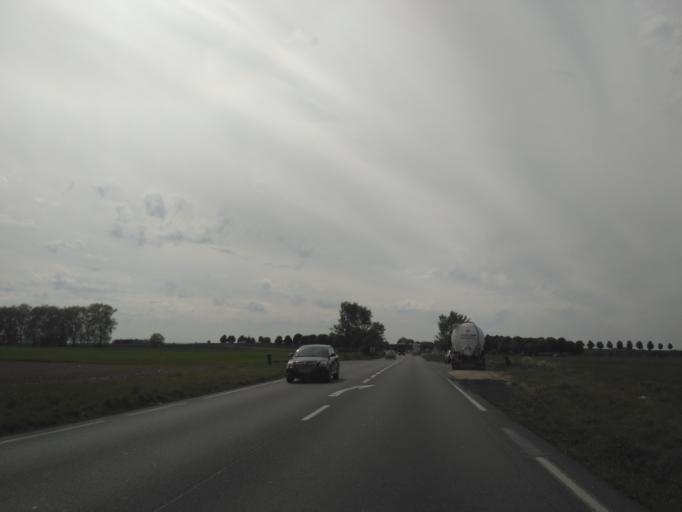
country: FR
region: Ile-de-France
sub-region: Departement de Seine-et-Marne
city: Moissy-Cramayel
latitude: 48.6317
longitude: 2.6355
